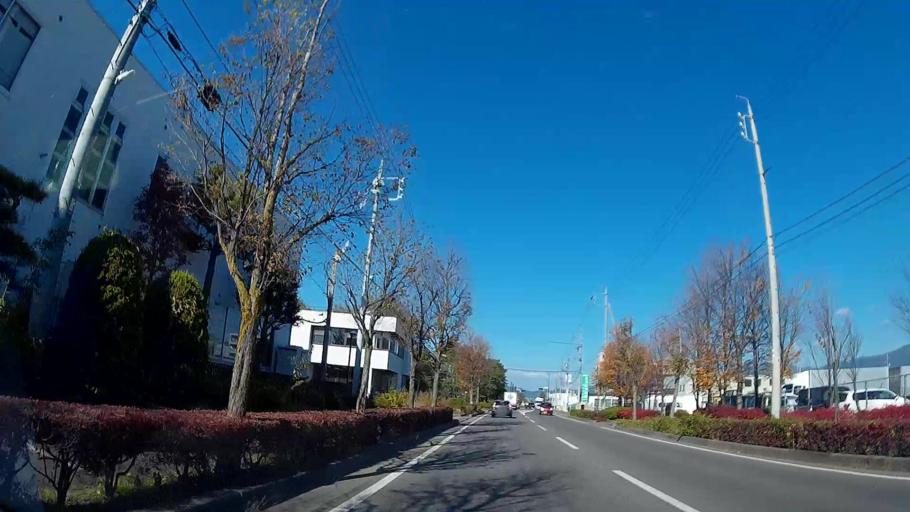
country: JP
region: Nagano
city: Matsumoto
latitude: 36.1916
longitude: 137.9493
